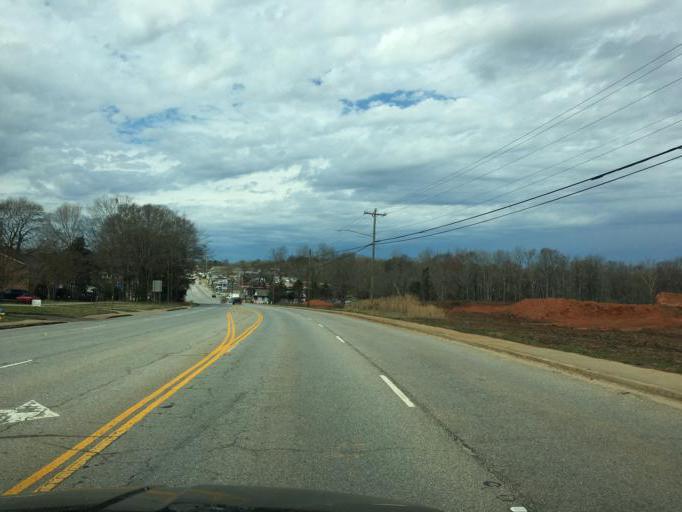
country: US
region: South Carolina
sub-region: Greenville County
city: Fountain Inn
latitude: 34.7008
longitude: -82.2129
